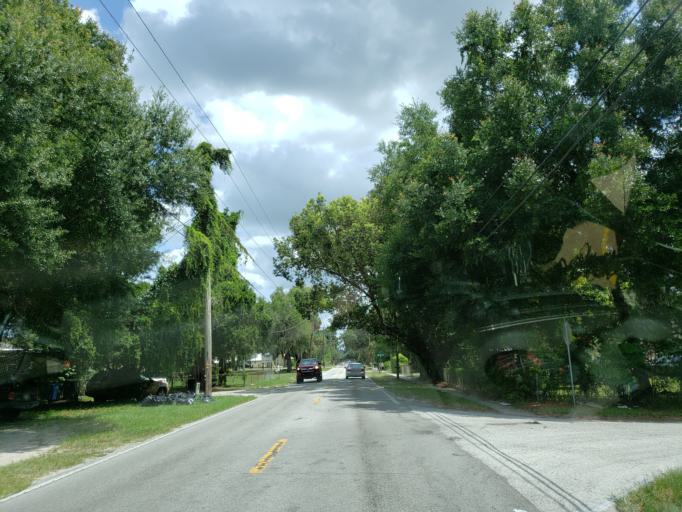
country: US
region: Florida
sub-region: Hillsborough County
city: Seffner
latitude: 27.9900
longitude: -82.2777
